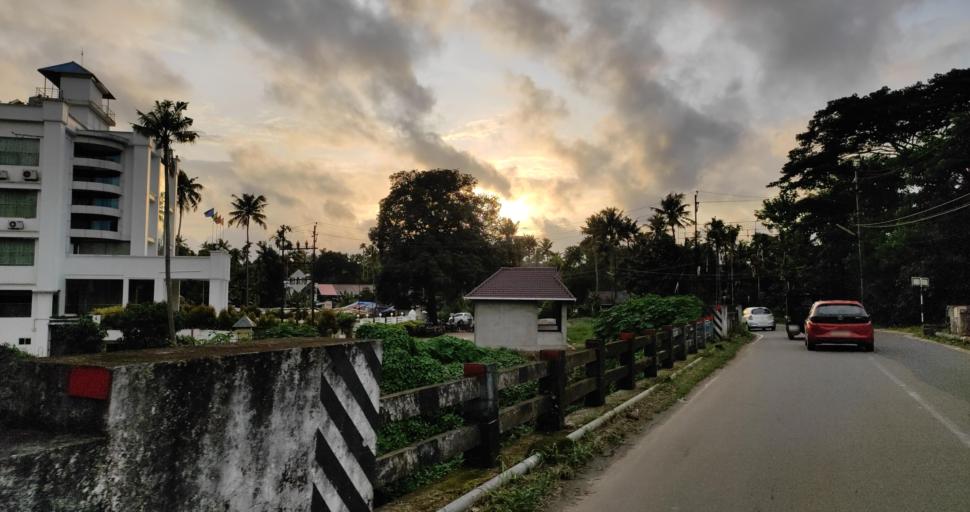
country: IN
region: Kerala
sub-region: Thrissur District
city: Kizhake Chalakudi
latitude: 10.3216
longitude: 76.3772
